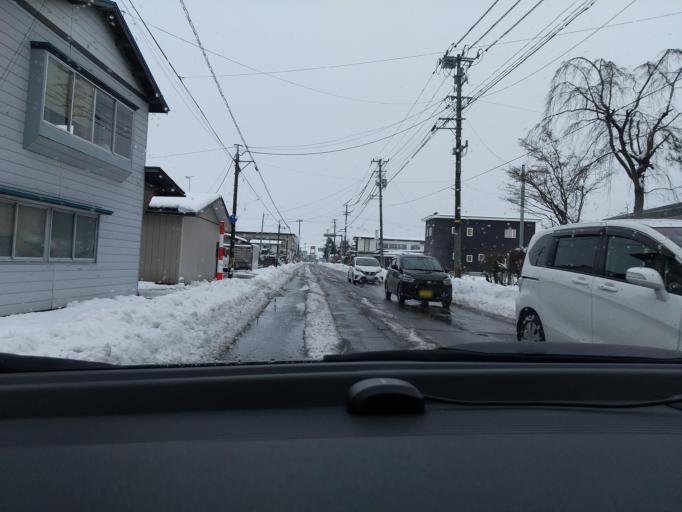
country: JP
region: Akita
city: Omagari
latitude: 39.4497
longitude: 140.4785
